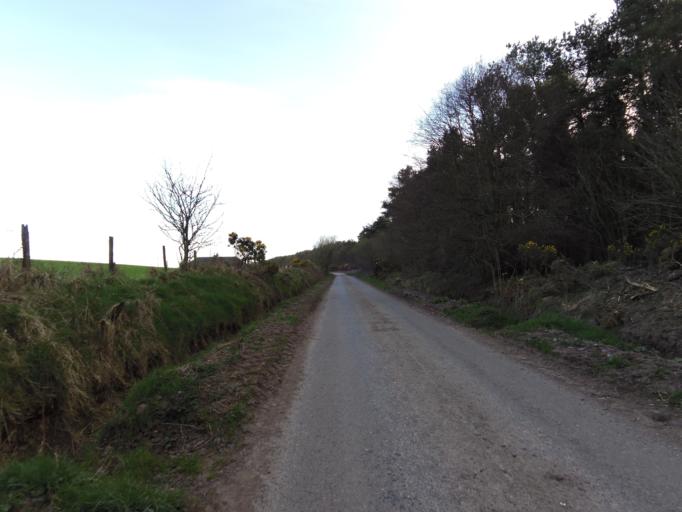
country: GB
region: Scotland
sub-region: Aberdeenshire
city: Stonehaven
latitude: 56.9275
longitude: -2.2284
